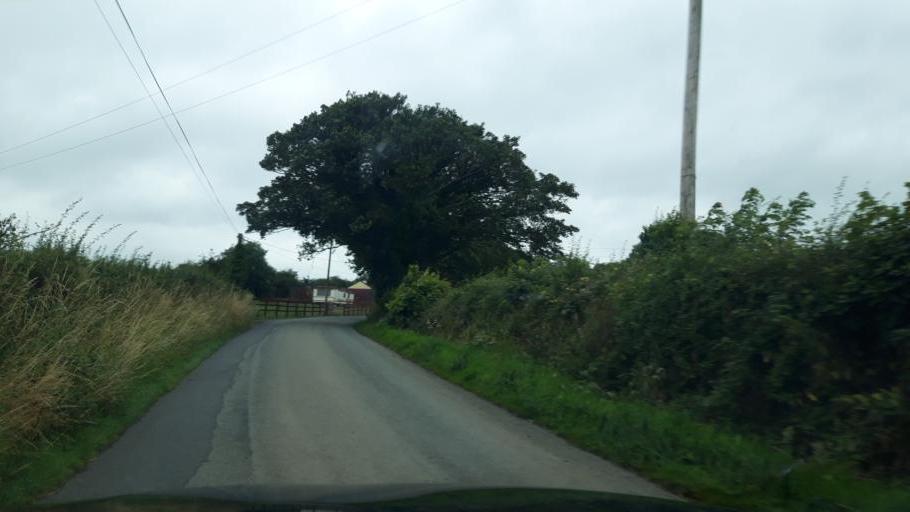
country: IE
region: Leinster
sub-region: Kilkenny
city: Ballyragget
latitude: 52.6996
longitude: -7.4117
